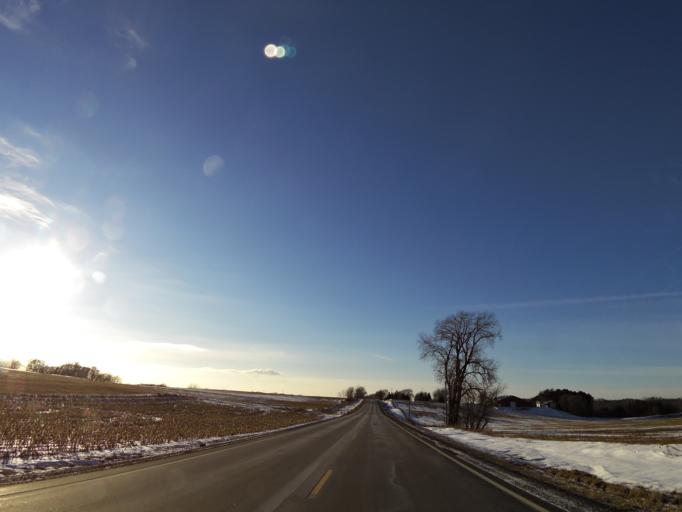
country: US
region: Minnesota
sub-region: Dakota County
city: Hastings
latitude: 44.7901
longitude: -92.8561
